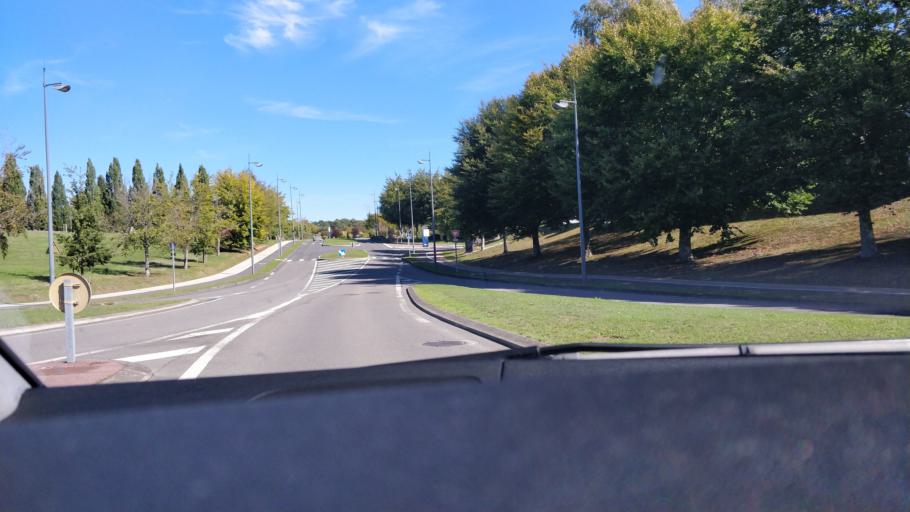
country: FR
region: Limousin
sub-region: Departement de la Haute-Vienne
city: Le Palais-sur-Vienne
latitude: 45.8593
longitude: 1.2893
